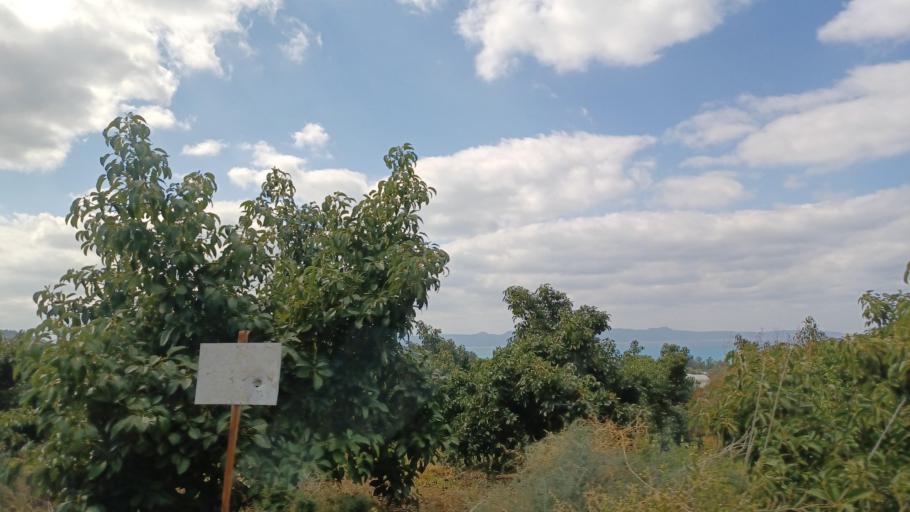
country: CY
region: Pafos
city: Polis
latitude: 35.1064
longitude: 32.5138
